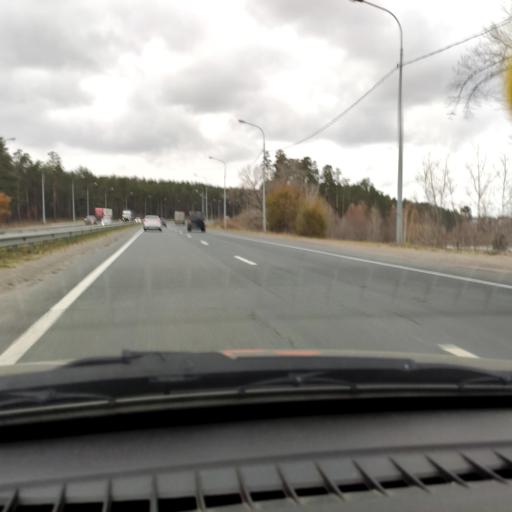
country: RU
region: Samara
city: Zhigulevsk
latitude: 53.5309
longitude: 49.5192
